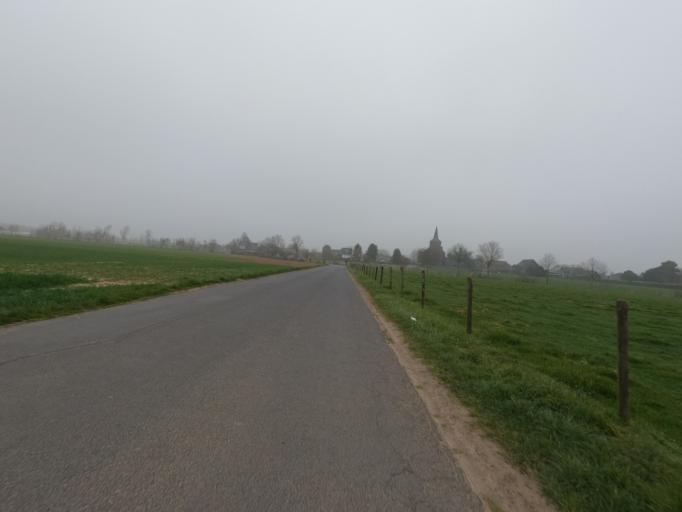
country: NL
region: Limburg
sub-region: Gemeente Roerdalen
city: Vlodrop
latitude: 51.1126
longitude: 6.0938
